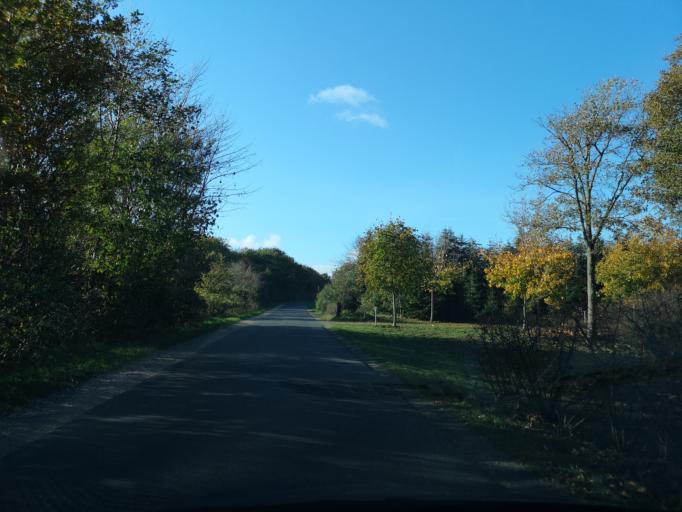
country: DK
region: Central Jutland
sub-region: Ringkobing-Skjern Kommune
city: Tarm
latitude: 55.8175
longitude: 8.4157
